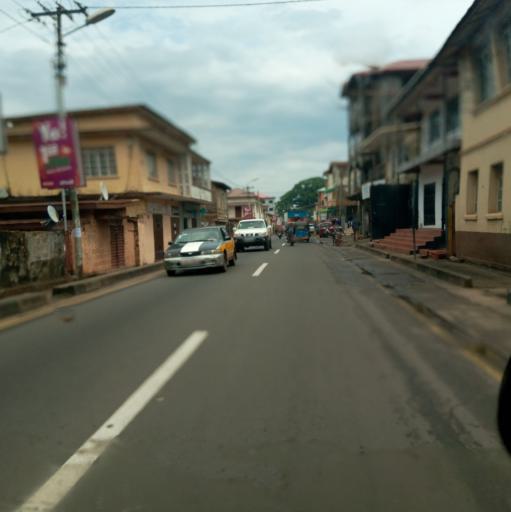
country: SL
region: Western Area
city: Freetown
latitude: 8.4835
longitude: -13.2359
